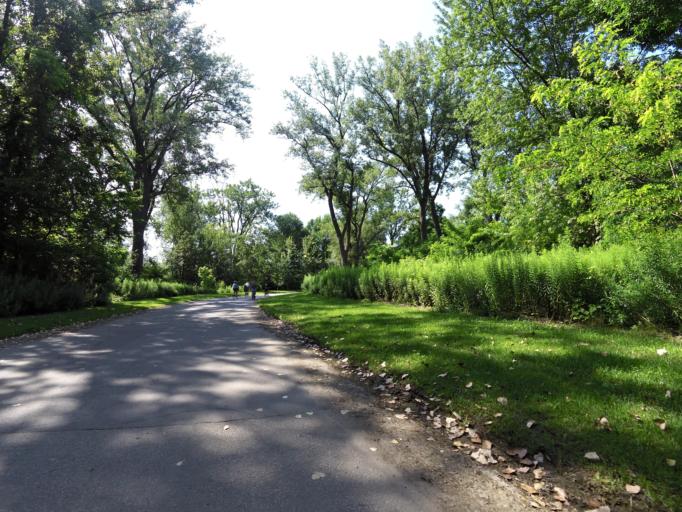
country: CA
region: Ontario
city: Toronto
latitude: 43.6162
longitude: -79.3894
